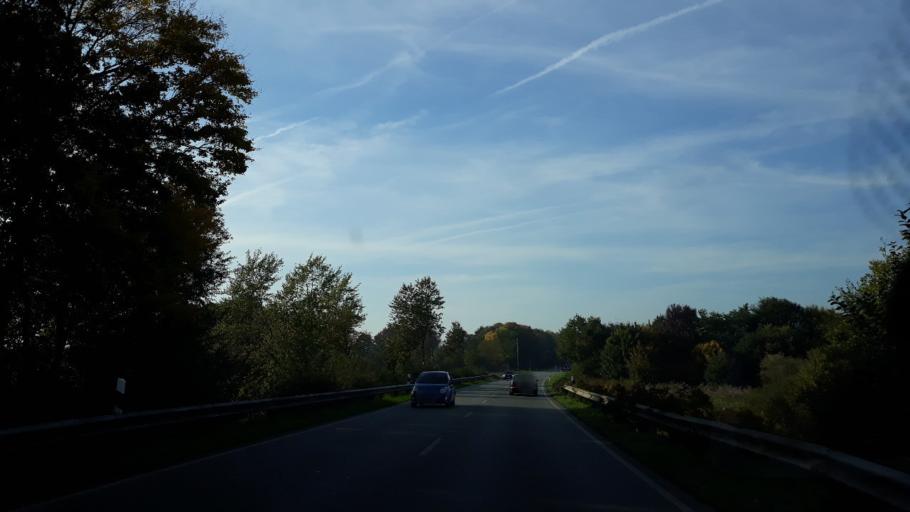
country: DE
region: Schleswig-Holstein
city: Schleswig
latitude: 54.5310
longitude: 9.5709
